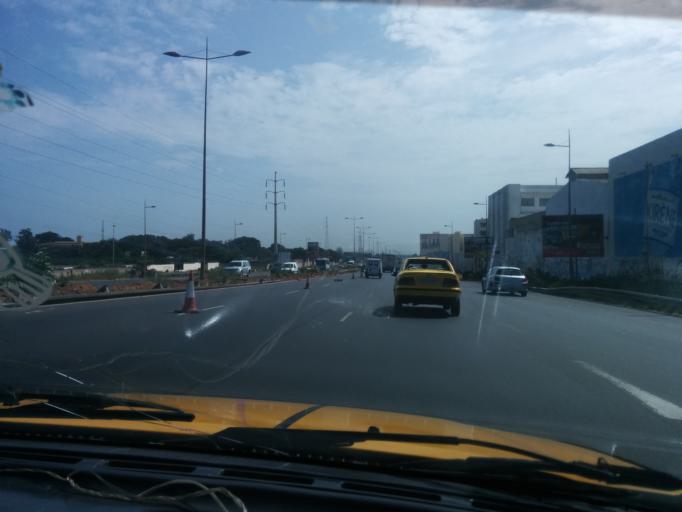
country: SN
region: Dakar
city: Grand Dakar
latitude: 14.7241
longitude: -17.4407
